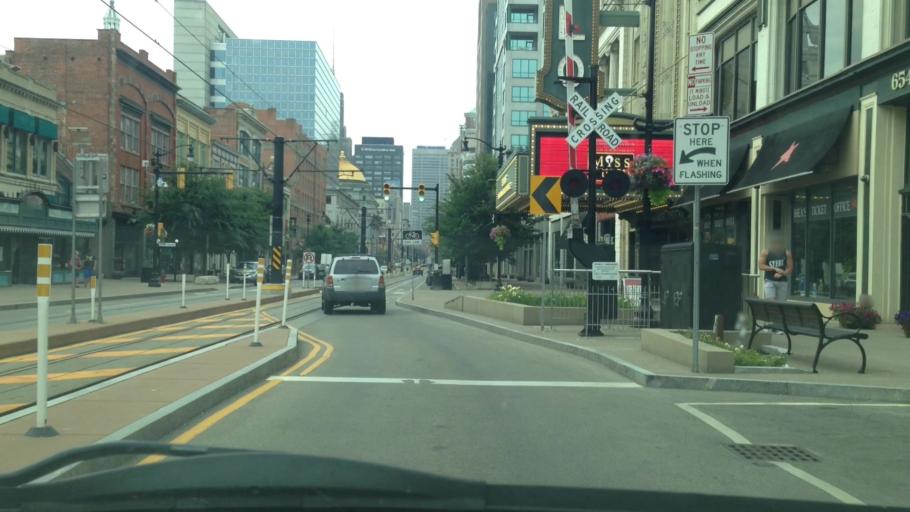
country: US
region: New York
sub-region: Erie County
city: Buffalo
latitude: 42.8918
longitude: -78.8724
